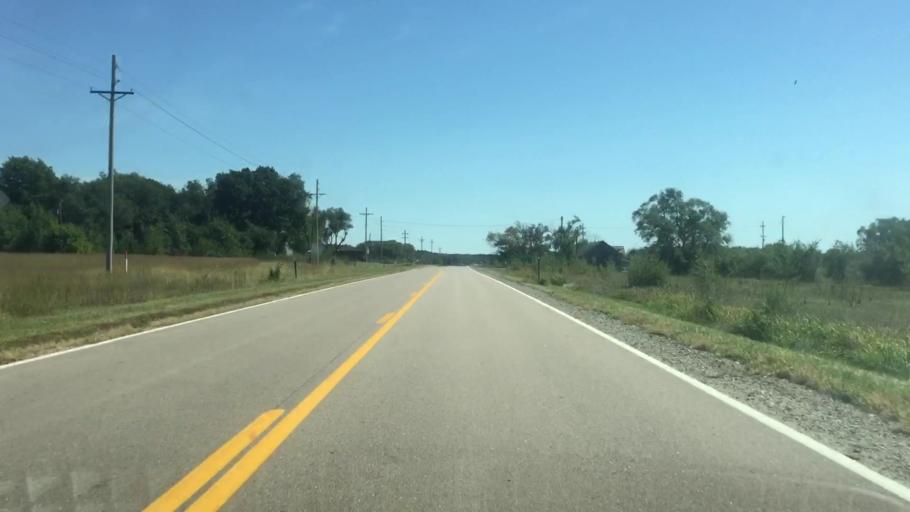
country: US
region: Nebraska
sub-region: Jefferson County
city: Fairbury
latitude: 40.0806
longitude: -97.1009
